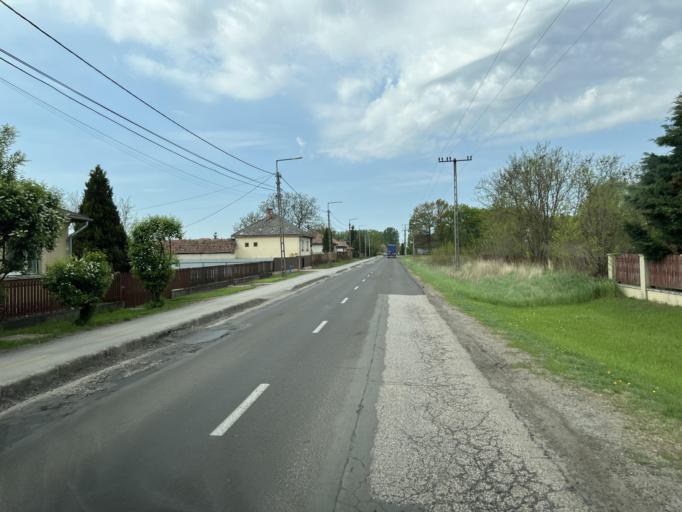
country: HU
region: Pest
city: Farmos
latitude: 47.3691
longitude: 19.8601
